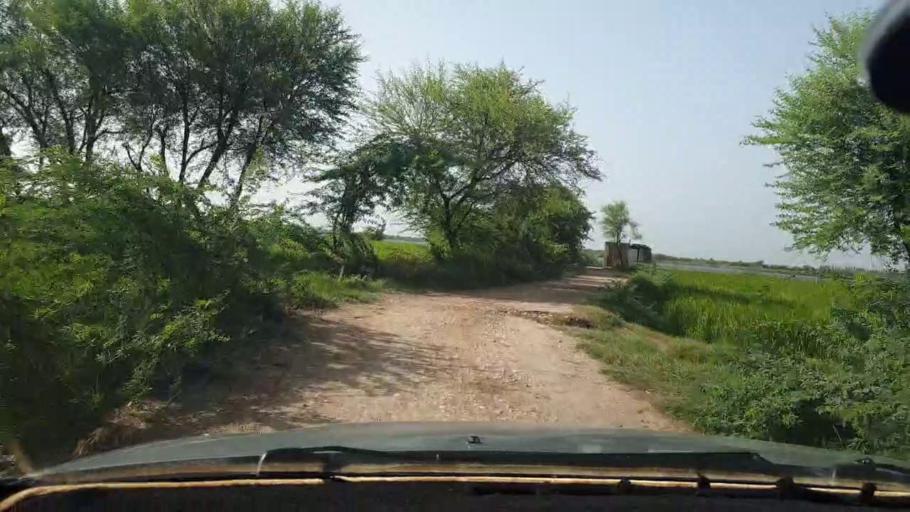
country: PK
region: Sindh
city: Tando Bago
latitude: 24.8060
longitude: 68.9166
